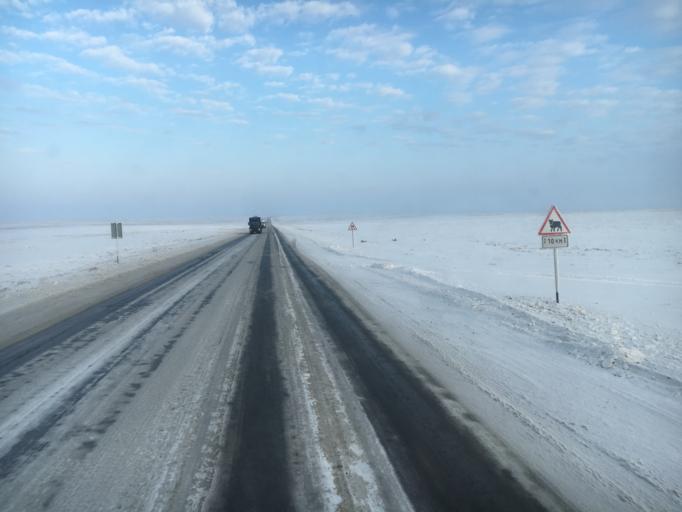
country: KZ
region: Qyzylorda
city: Sekseuil
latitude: 47.8011
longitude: 61.3441
